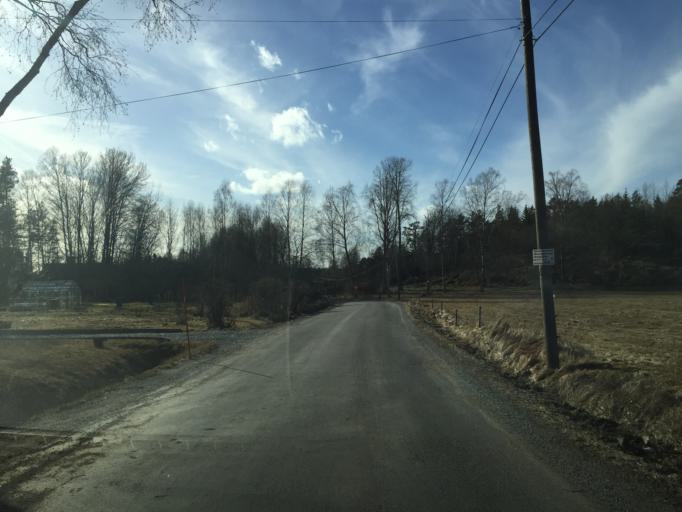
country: SE
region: Stockholm
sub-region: Nynashamns Kommun
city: Osmo
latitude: 59.0453
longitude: 17.8248
